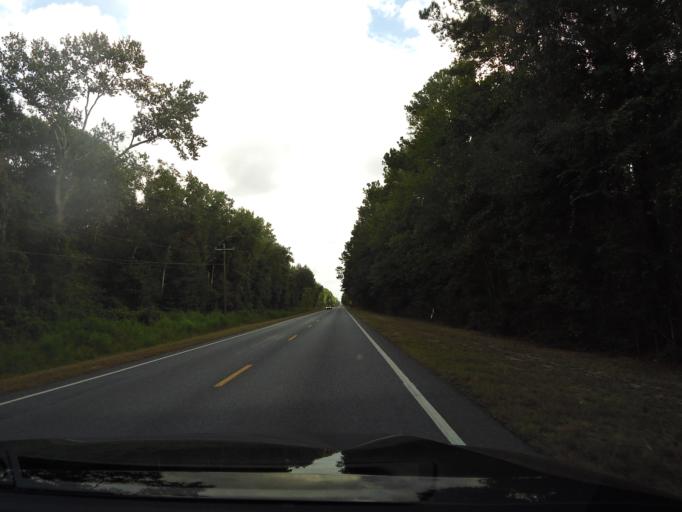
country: US
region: Georgia
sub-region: Liberty County
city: Midway
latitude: 31.6980
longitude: -81.4122
